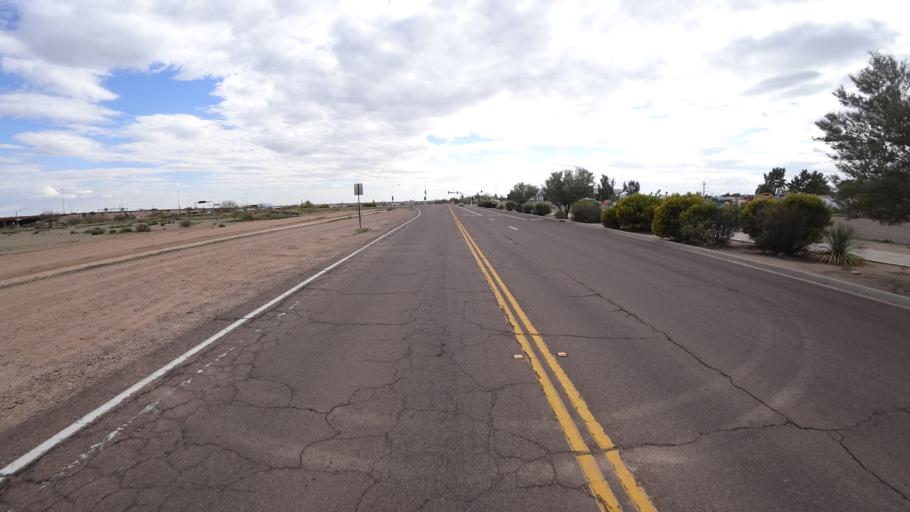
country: US
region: Arizona
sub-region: Maricopa County
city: Scottsdale
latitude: 33.4673
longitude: -111.8919
